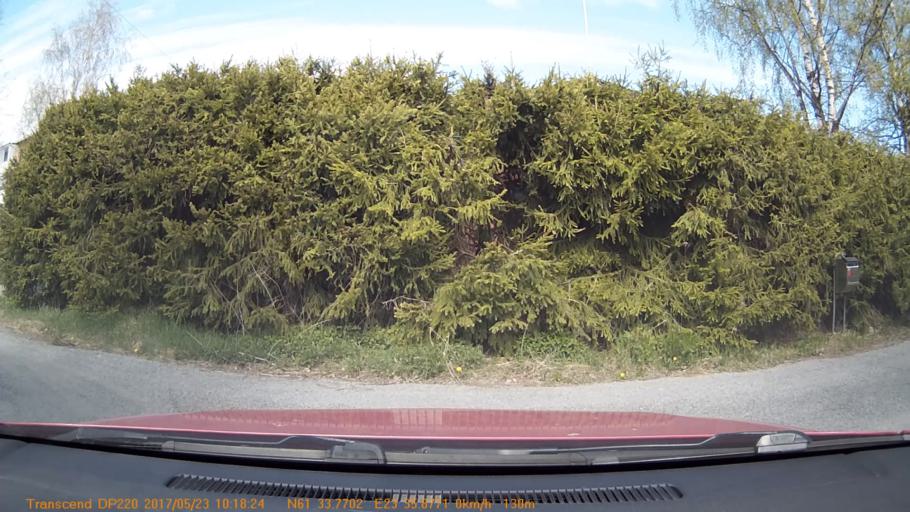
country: FI
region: Pirkanmaa
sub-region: Tampere
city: Yloejaervi
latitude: 61.5628
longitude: 23.5980
